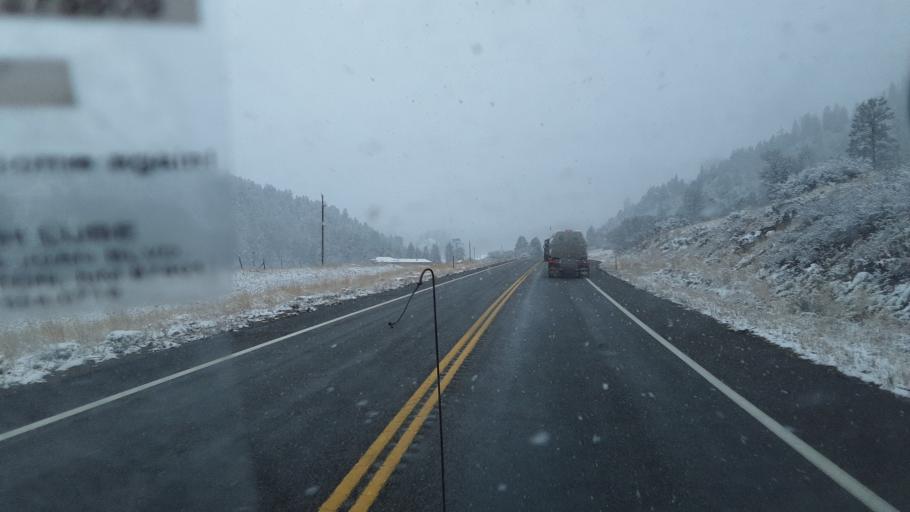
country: US
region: Colorado
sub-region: La Plata County
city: Bayfield
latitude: 37.2295
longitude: -107.3871
